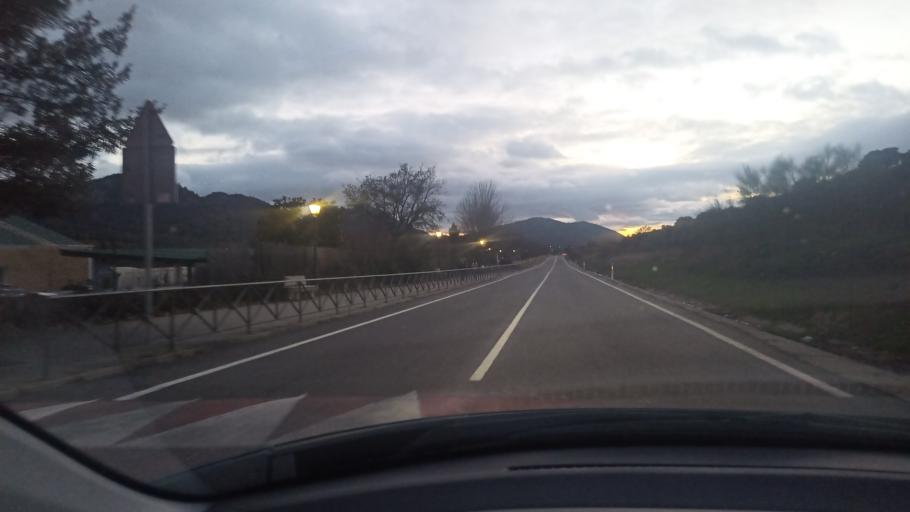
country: ES
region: Madrid
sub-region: Provincia de Madrid
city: Robledo de Chavela
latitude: 40.4960
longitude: -4.2411
